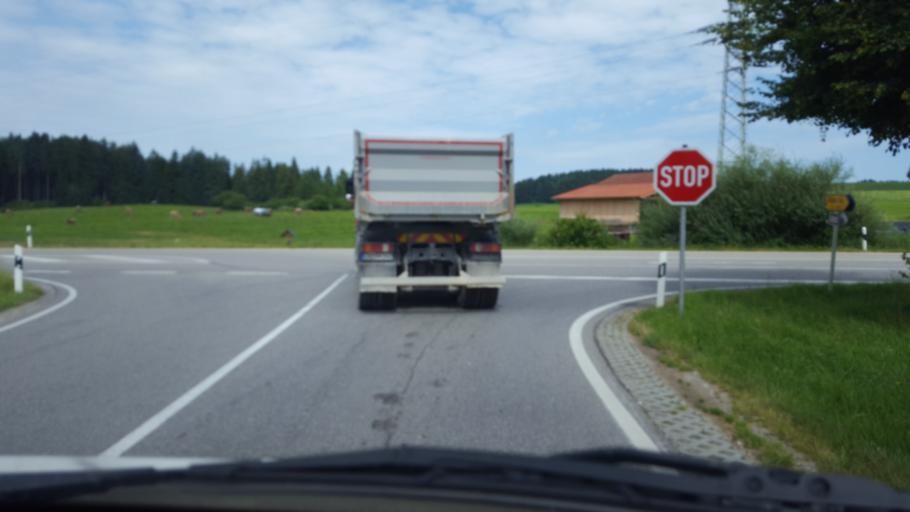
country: DE
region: Bavaria
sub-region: Swabia
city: Nesselwang
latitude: 47.6363
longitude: 10.5259
